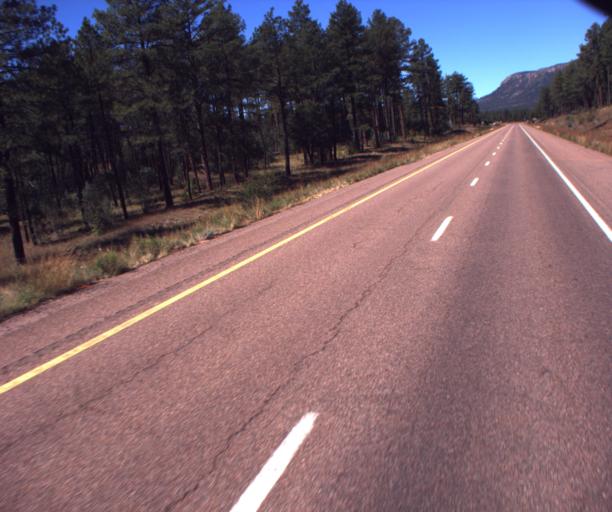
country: US
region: Arizona
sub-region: Gila County
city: Star Valley
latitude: 34.3030
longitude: -110.9905
